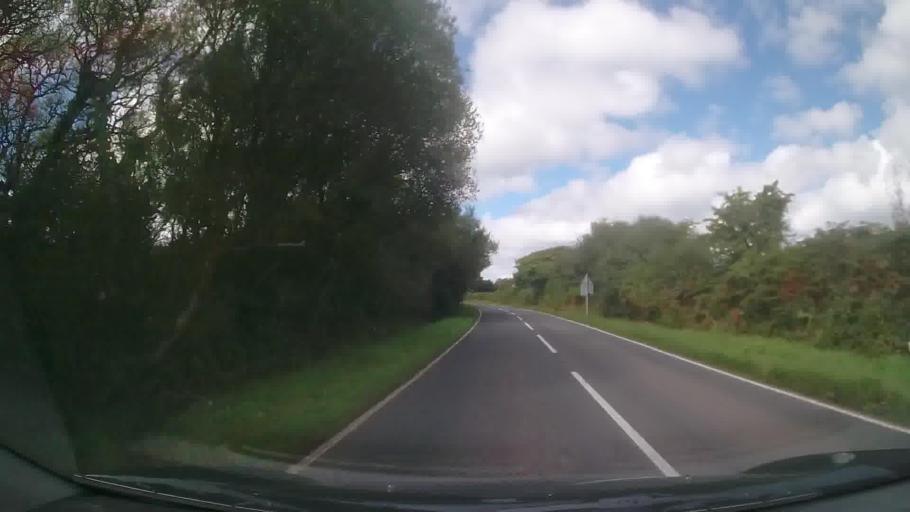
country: GB
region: Wales
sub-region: Pembrokeshire
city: Manorbier
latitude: 51.6517
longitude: -4.7711
